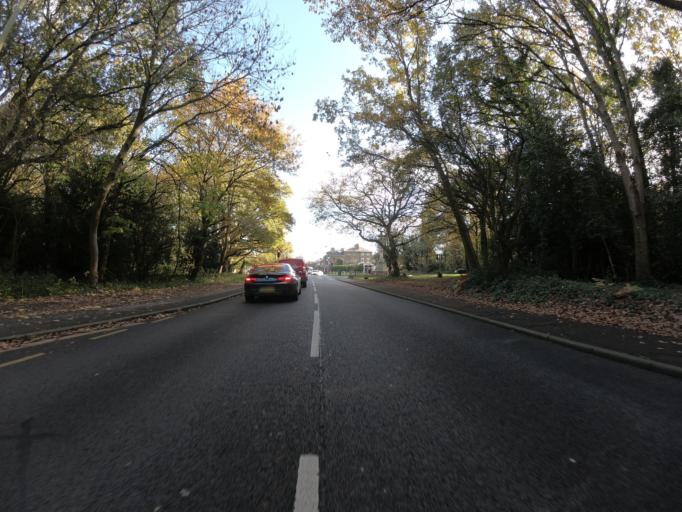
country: GB
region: England
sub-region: Greater London
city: Chislehurst
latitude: 51.4129
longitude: 0.0736
